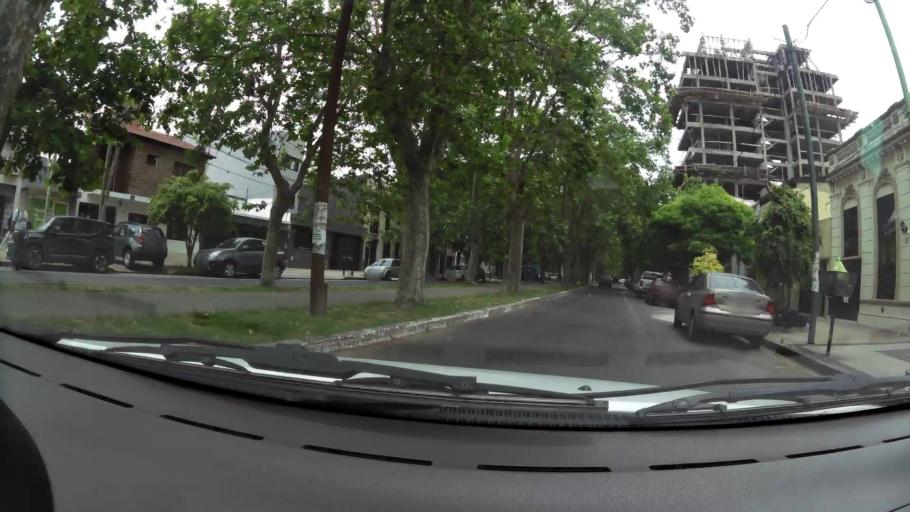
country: AR
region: Buenos Aires
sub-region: Partido de La Plata
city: La Plata
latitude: -34.9276
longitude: -57.9626
